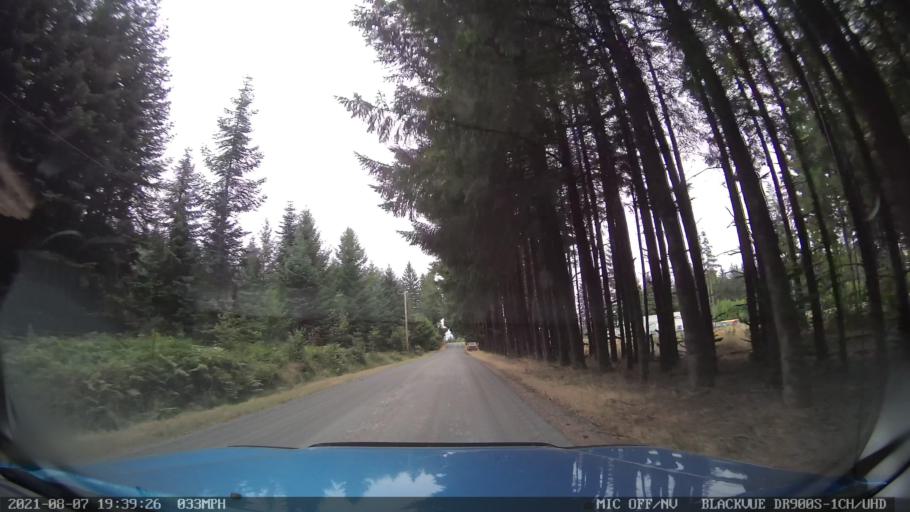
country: US
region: Oregon
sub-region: Marion County
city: Silverton
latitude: 44.9361
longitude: -122.6569
